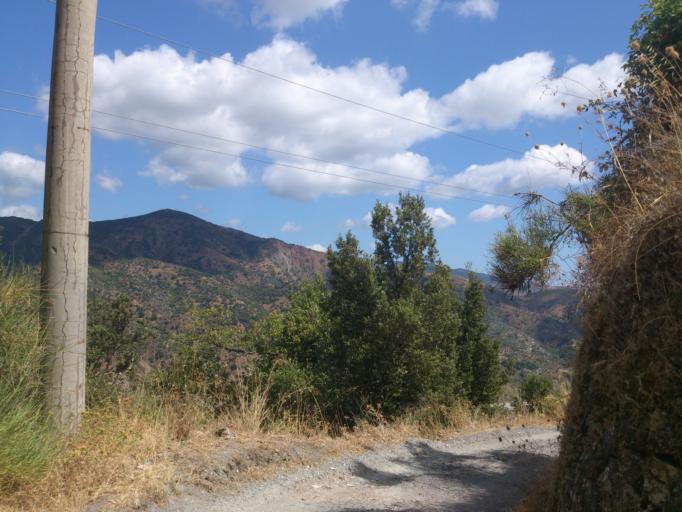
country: IT
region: Calabria
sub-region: Provincia di Reggio Calabria
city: Pazzano
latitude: 38.4751
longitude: 16.4439
